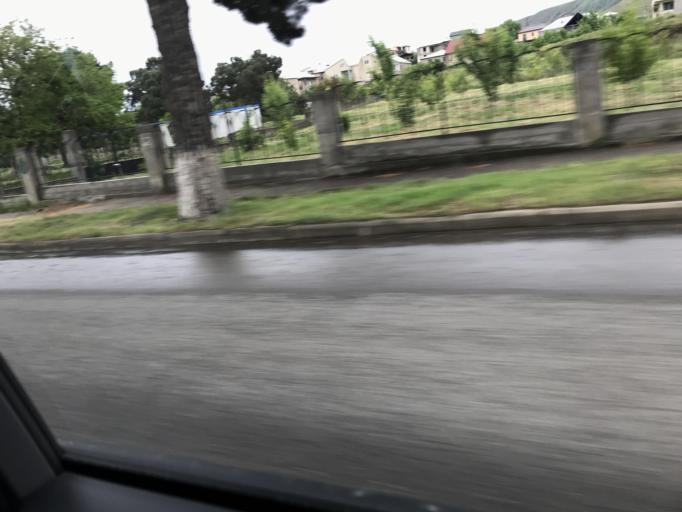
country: GE
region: Kvemo Kartli
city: Rust'avi
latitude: 41.5514
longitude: 44.9797
